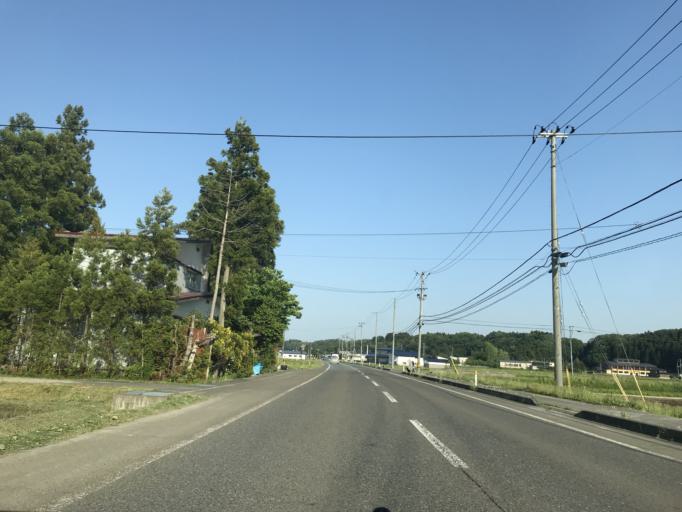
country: JP
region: Iwate
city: Kitakami
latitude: 39.2867
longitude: 141.0055
